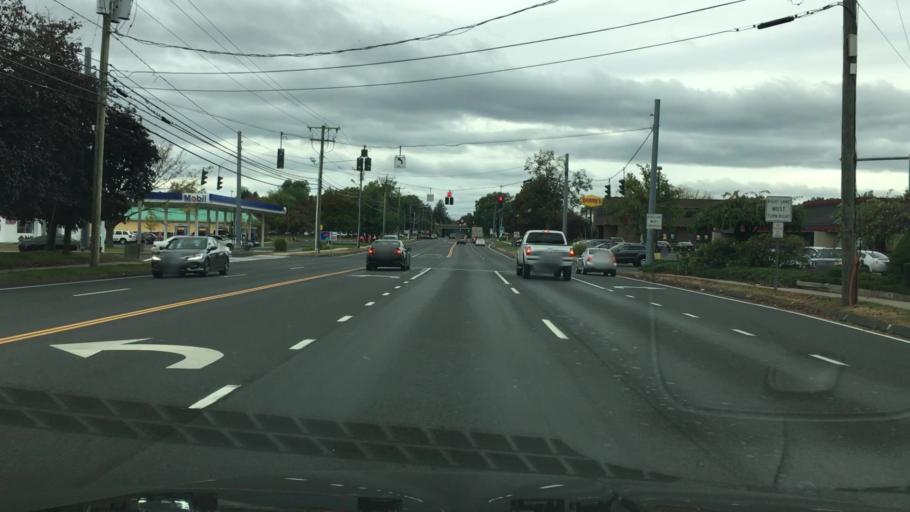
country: US
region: Connecticut
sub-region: Hartford County
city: Thompsonville
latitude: 41.9981
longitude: -72.5804
